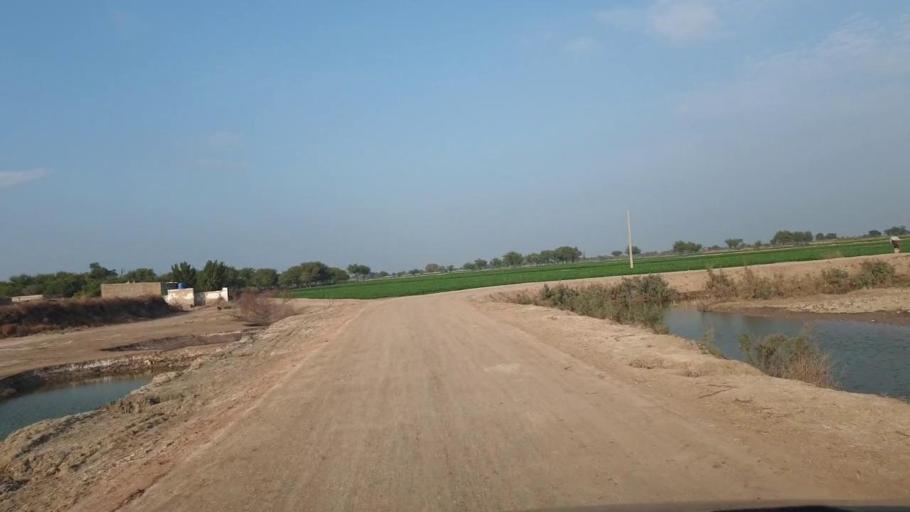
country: PK
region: Sindh
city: Shahdadpur
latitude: 25.8825
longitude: 68.7273
